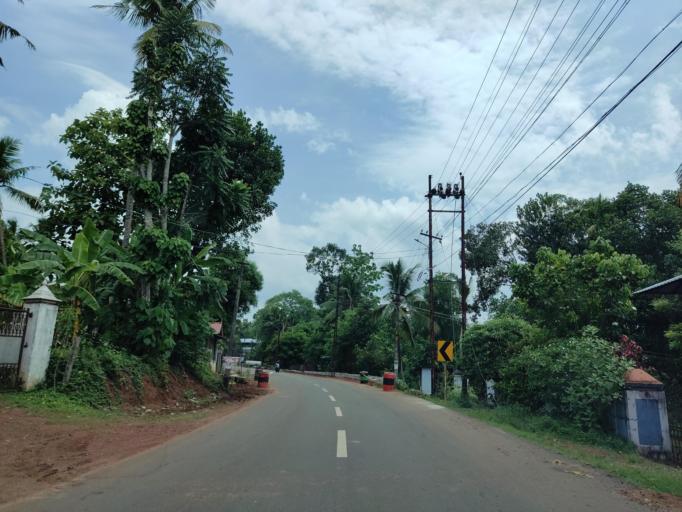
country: IN
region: Kerala
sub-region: Alappuzha
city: Mavelikara
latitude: 9.2302
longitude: 76.6067
